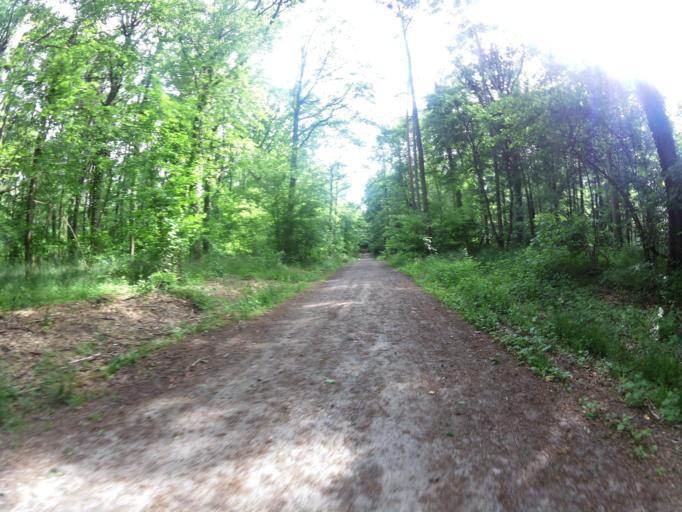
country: DE
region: Bavaria
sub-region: Regierungsbezirk Unterfranken
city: Ochsenfurt
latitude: 49.6896
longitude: 10.0725
